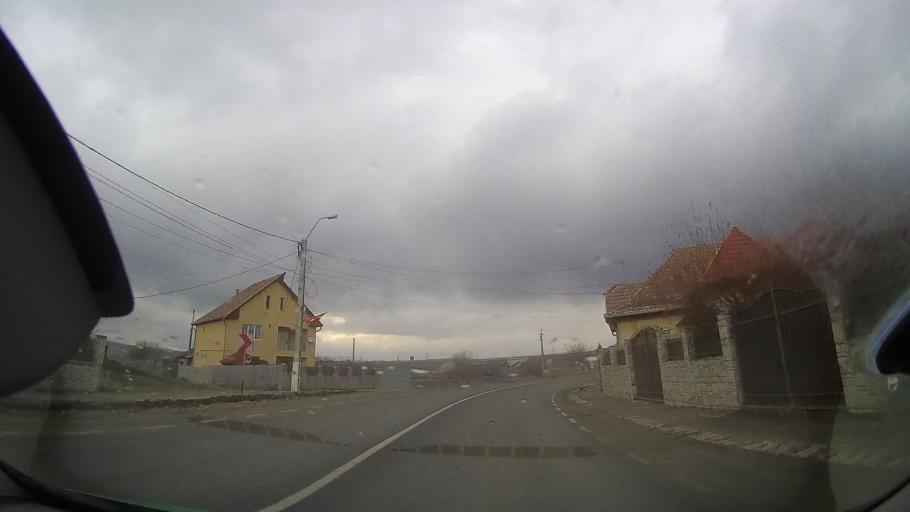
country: RO
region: Cluj
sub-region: Comuna Mihai Viteazu
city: Mihai Viteazu
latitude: 46.5417
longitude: 23.7707
